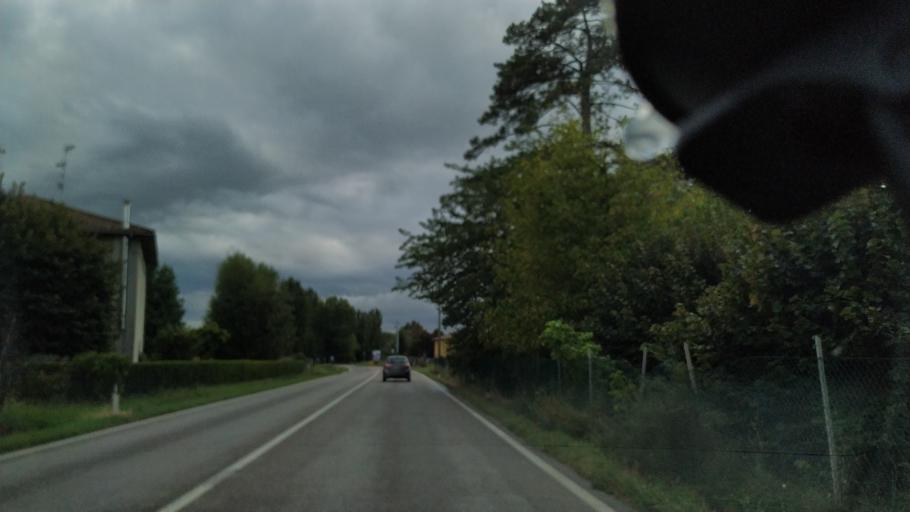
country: IT
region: Emilia-Romagna
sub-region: Provincia di Ferrara
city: Dosso
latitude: 44.7774
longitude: 11.3548
